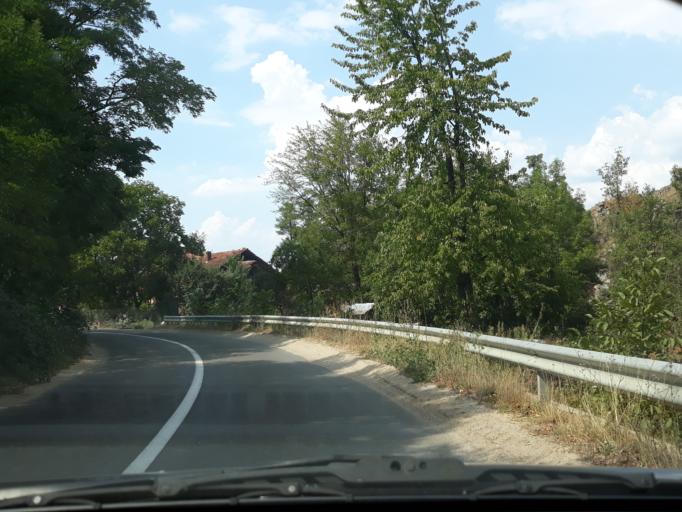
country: RO
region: Bihor
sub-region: Comuna Pietroasa
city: Pietroasa
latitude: 46.5898
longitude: 22.5629
